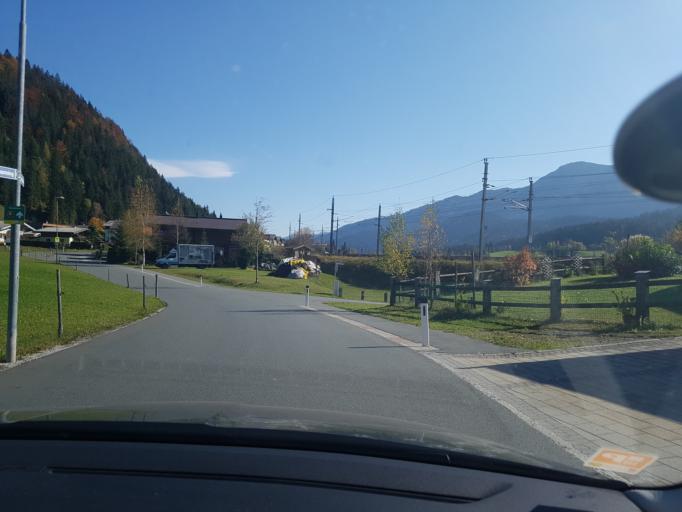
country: AT
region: Tyrol
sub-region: Politischer Bezirk Kitzbuhel
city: Hochfilzen
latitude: 47.4753
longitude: 12.6155
